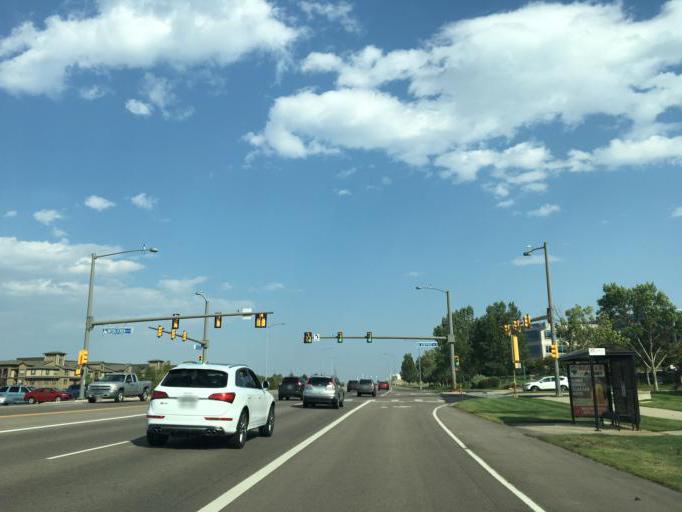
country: US
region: Colorado
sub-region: Broomfield County
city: Broomfield
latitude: 39.9161
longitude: -105.1065
